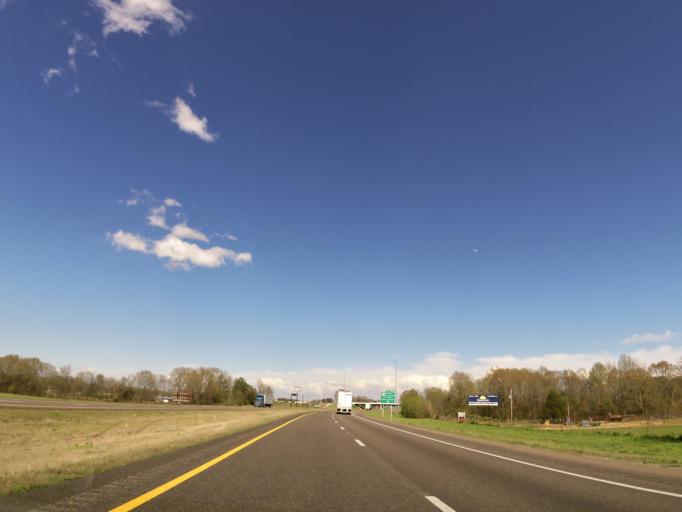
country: US
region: Tennessee
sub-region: Henderson County
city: Lexington
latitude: 35.7875
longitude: -88.3986
